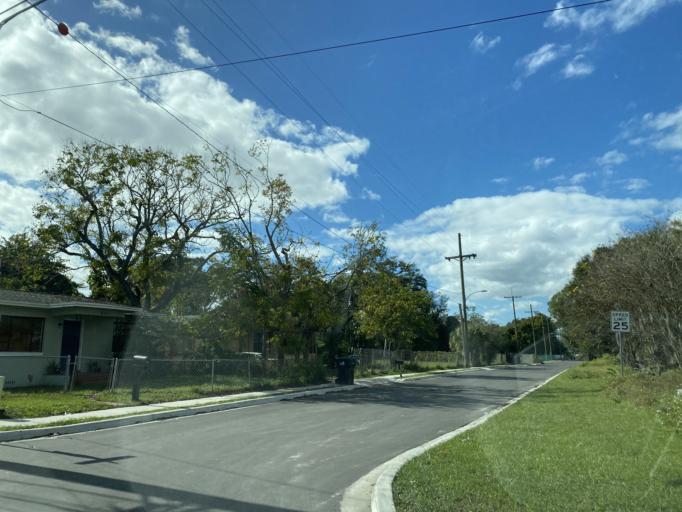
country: US
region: Florida
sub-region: Orange County
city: Orlando
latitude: 28.5238
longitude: -81.3930
